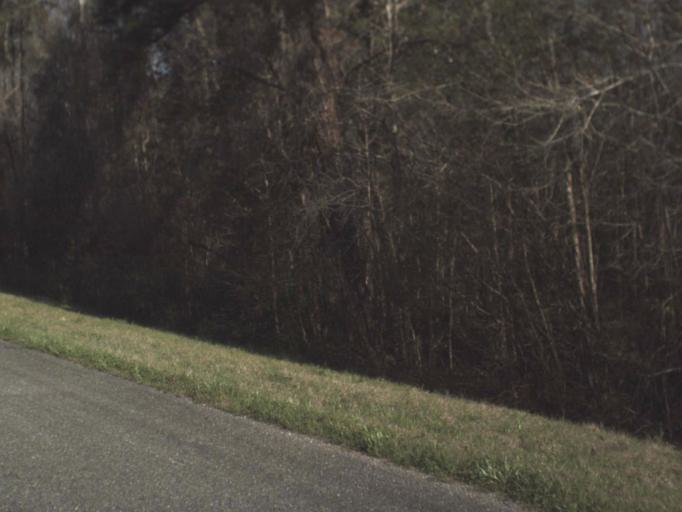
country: US
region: Florida
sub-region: Jefferson County
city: Monticello
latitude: 30.4810
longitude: -83.9443
